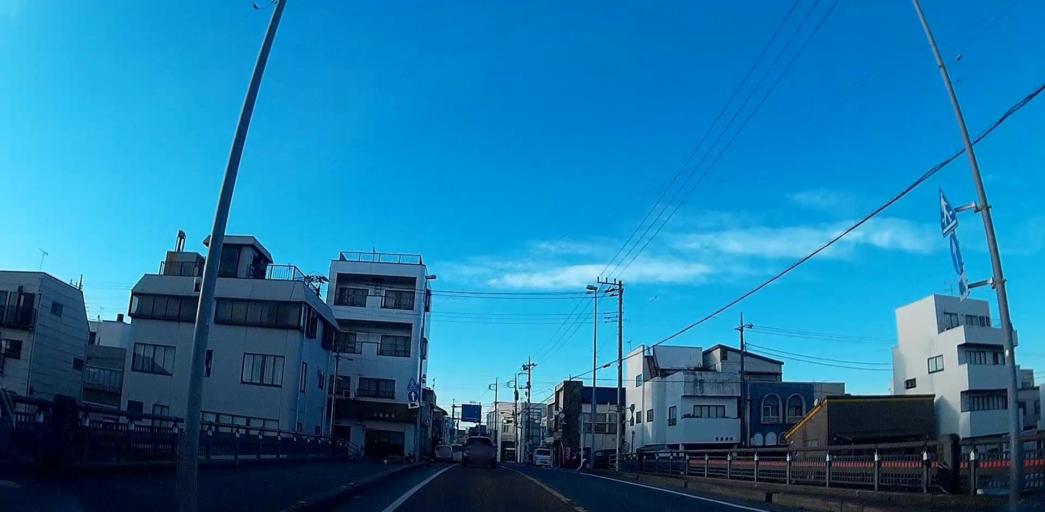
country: JP
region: Chiba
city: Omigawa
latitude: 35.8546
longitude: 140.6060
